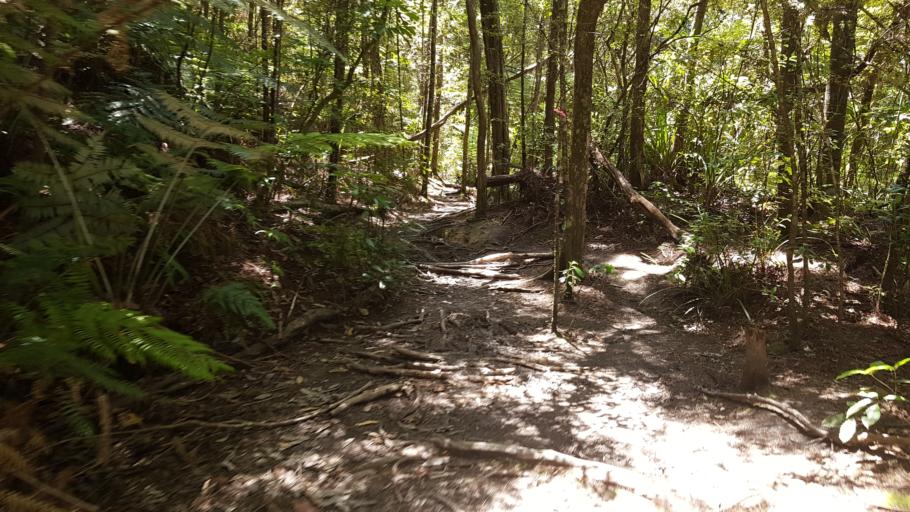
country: NZ
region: Auckland
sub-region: Auckland
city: North Shore
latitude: -36.8230
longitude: 174.7166
